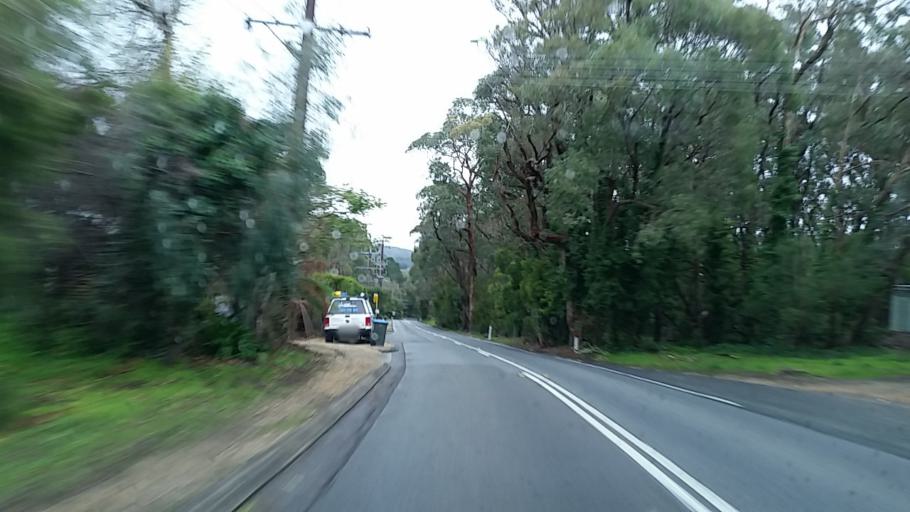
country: AU
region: South Australia
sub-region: Adelaide Hills
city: Bridgewater
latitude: -34.9884
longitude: 138.7255
